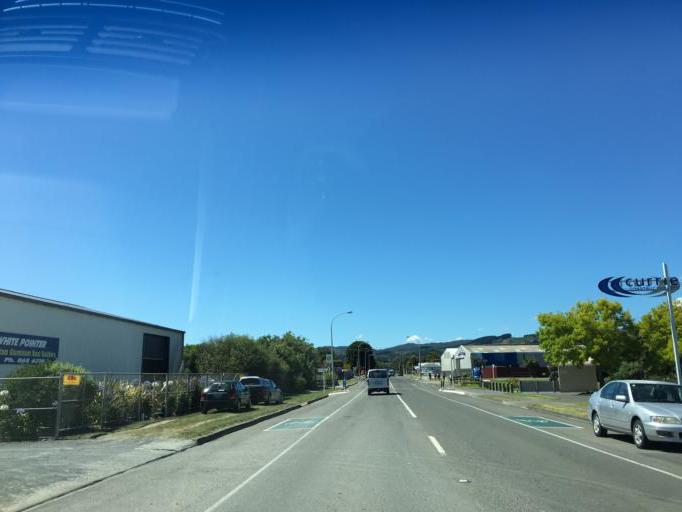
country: NZ
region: Gisborne
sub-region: Gisborne District
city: Gisborne
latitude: -38.6658
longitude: 178.0053
